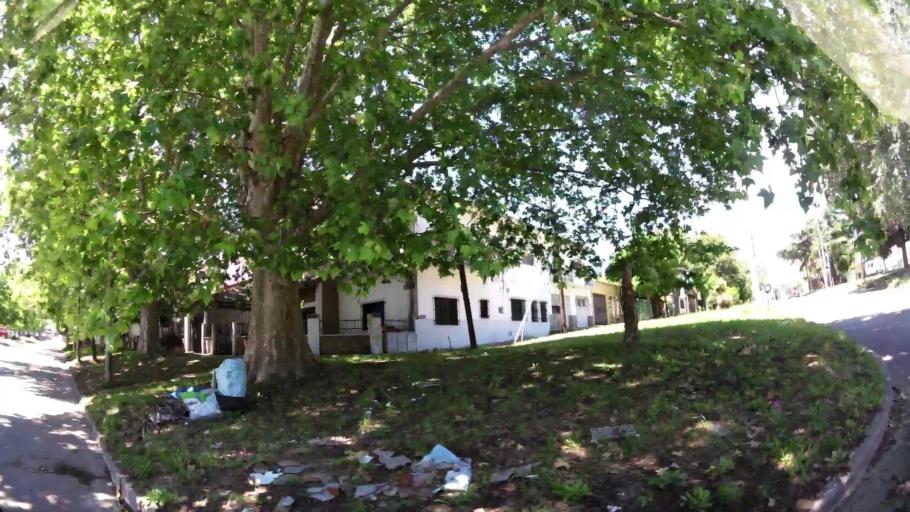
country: AR
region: Buenos Aires
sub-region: Partido de Quilmes
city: Quilmes
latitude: -34.7350
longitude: -58.2815
